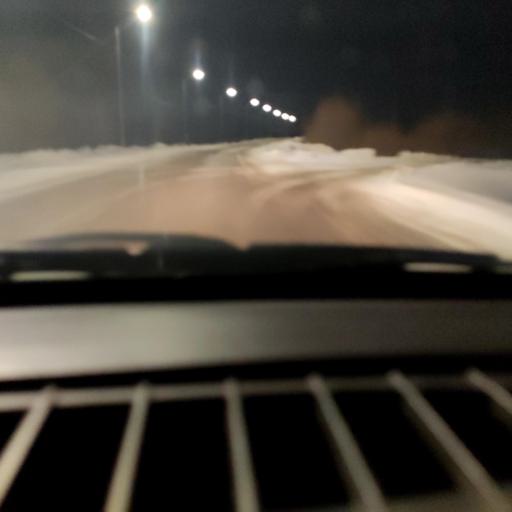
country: RU
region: Bashkortostan
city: Ulukulevo
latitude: 54.5654
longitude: 56.3383
